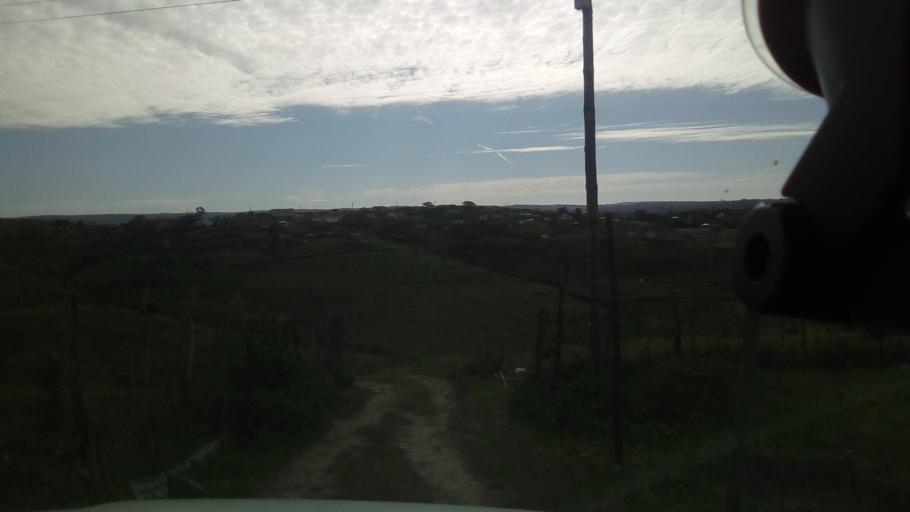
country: ZA
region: Eastern Cape
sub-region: Buffalo City Metropolitan Municipality
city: East London
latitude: -32.7987
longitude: 27.9585
